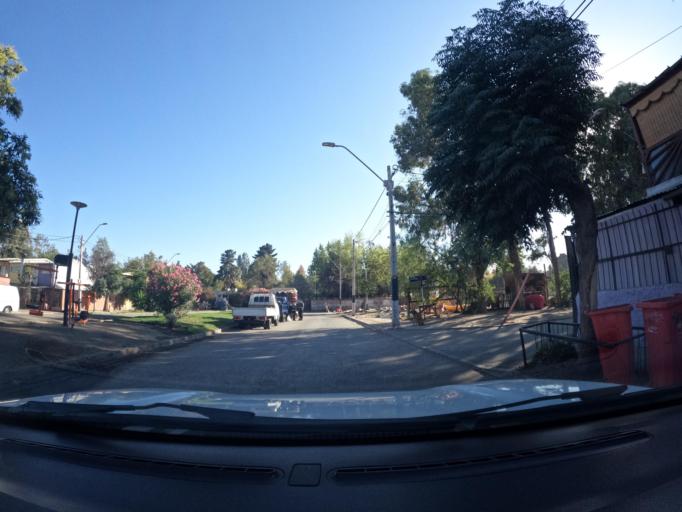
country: CL
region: Santiago Metropolitan
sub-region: Provincia de Santiago
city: Villa Presidente Frei, Nunoa, Santiago, Chile
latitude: -33.5005
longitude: -70.5732
